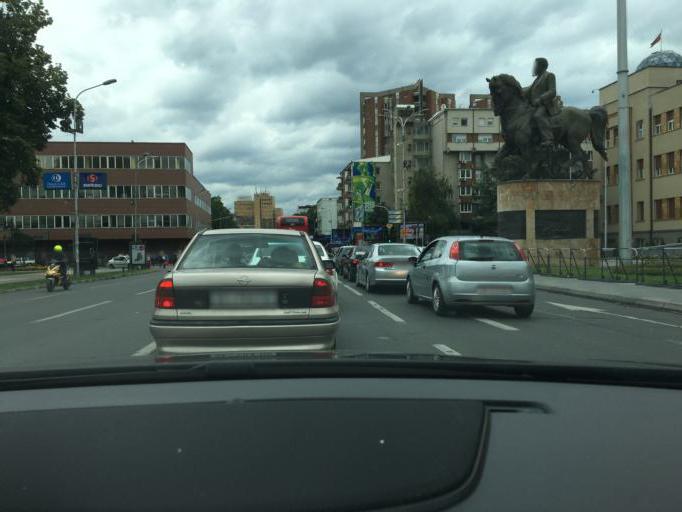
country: MK
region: Karpos
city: Skopje
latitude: 41.9934
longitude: 21.4331
